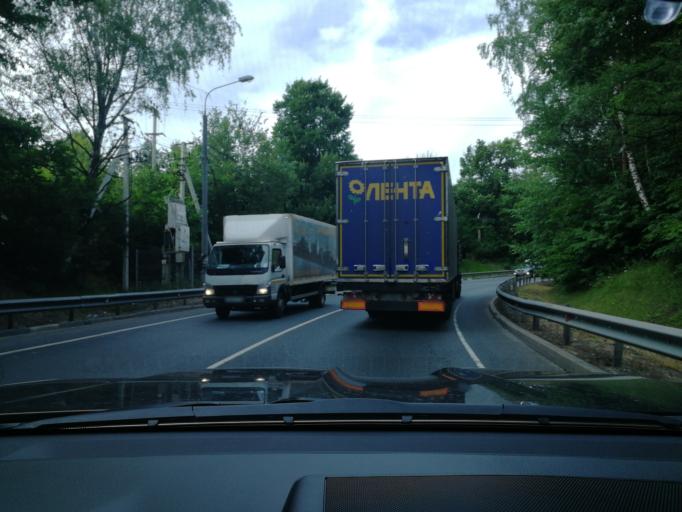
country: RU
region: Moskovskaya
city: Popovo
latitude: 55.0601
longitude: 37.7658
